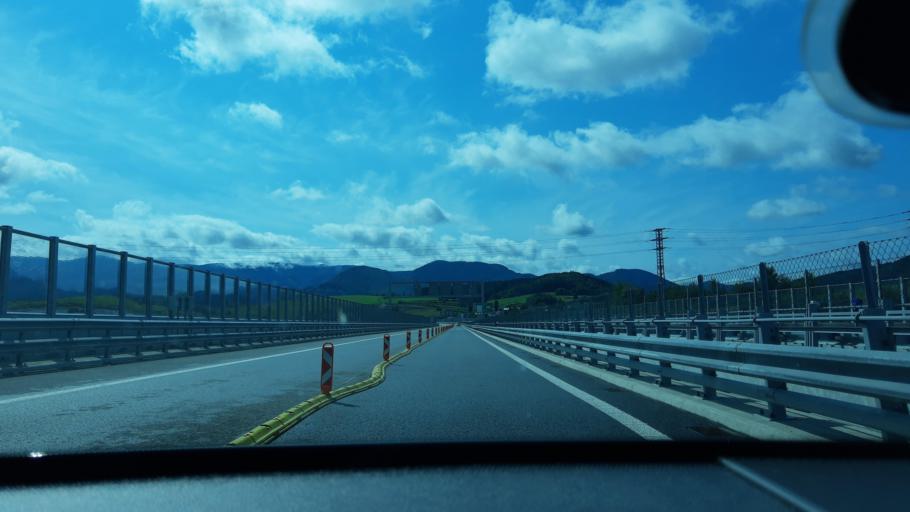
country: SK
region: Zilinsky
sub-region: Okres Zilina
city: Zilina
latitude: 49.1841
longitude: 18.7216
